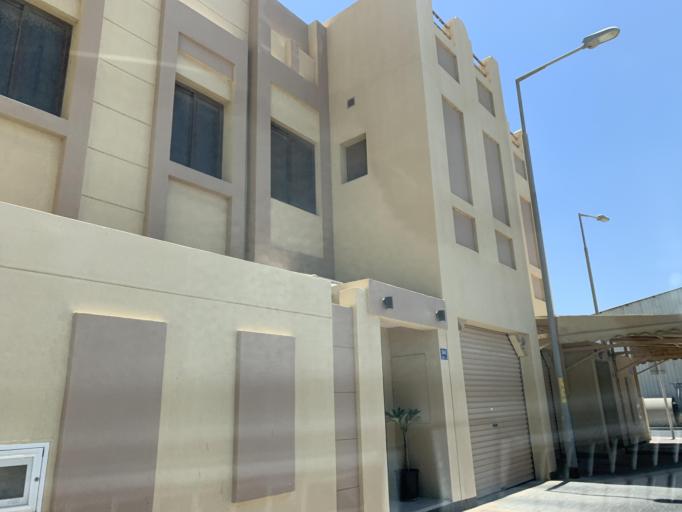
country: BH
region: Manama
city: Jidd Hafs
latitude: 26.2348
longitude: 50.4911
